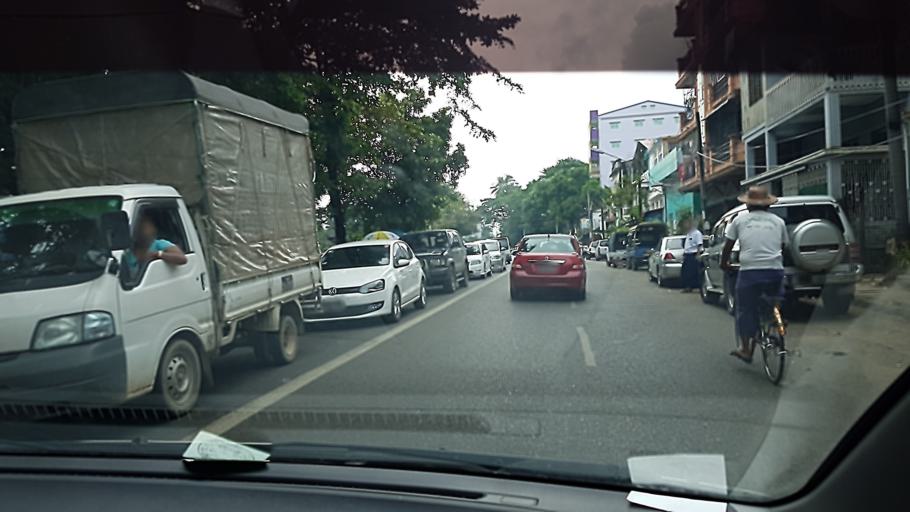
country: MM
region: Yangon
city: Yangon
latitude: 16.8022
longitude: 96.1260
